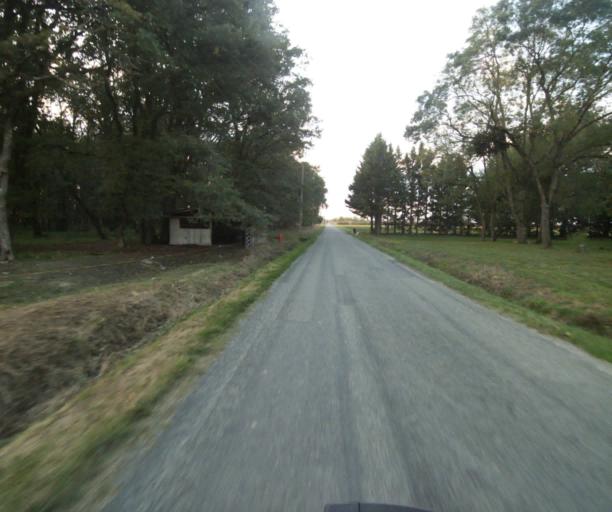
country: FR
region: Midi-Pyrenees
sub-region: Departement du Tarn-et-Garonne
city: Verdun-sur-Garonne
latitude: 43.8291
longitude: 1.2298
